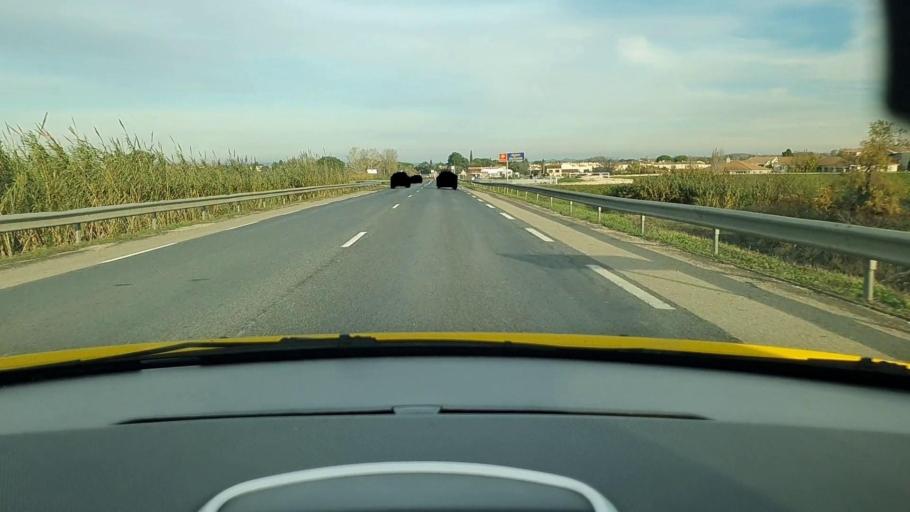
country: FR
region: Languedoc-Roussillon
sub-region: Departement du Gard
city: Fourques
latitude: 43.6877
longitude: 4.6055
